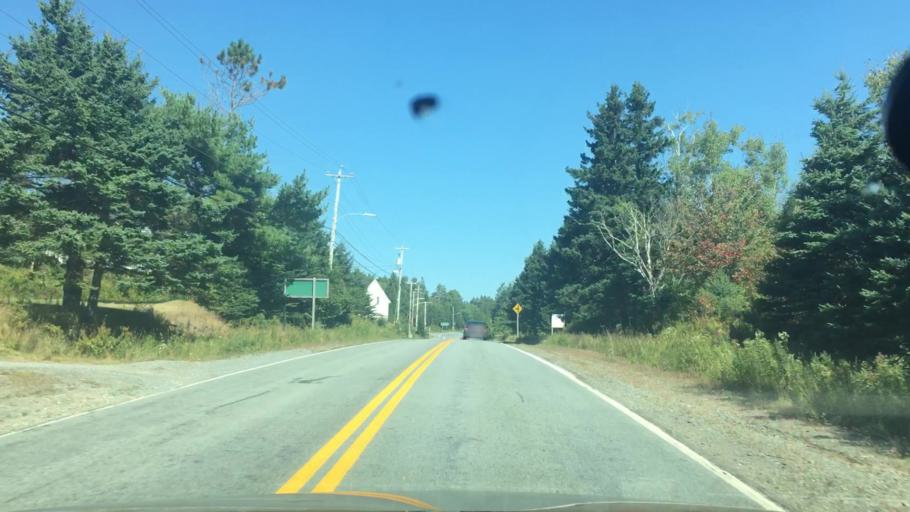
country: CA
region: Nova Scotia
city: New Glasgow
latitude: 44.9236
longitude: -62.5456
